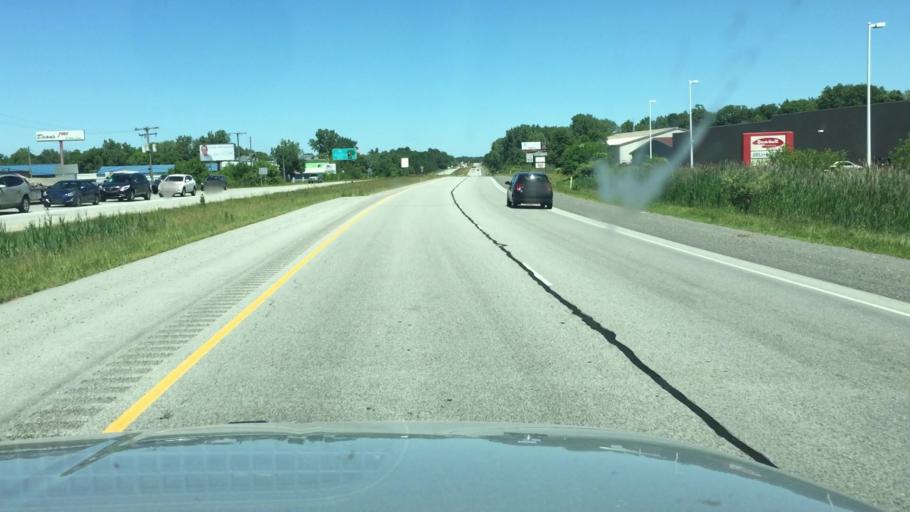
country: US
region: Indiana
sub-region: Porter County
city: Chesterton
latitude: 41.5944
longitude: -87.0454
